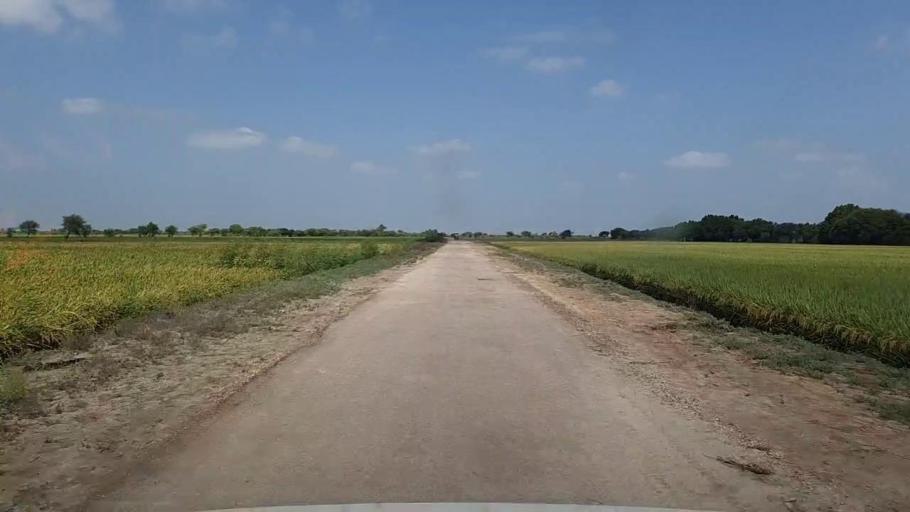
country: PK
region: Sindh
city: Kario
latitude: 24.6859
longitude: 68.5880
